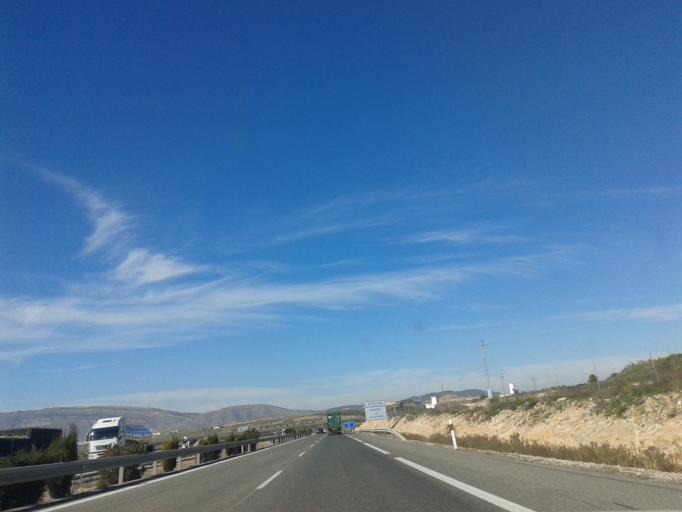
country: ES
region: Castille-La Mancha
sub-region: Provincia de Albacete
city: Caudete
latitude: 38.7016
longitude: -0.9216
